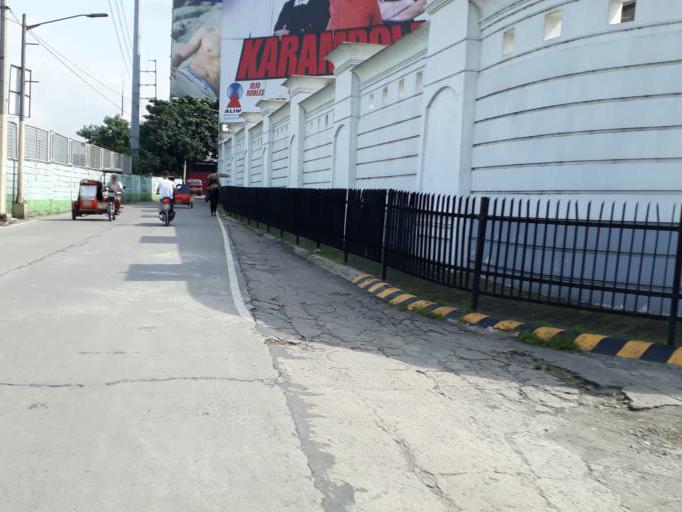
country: PH
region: Calabarzon
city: Bagong Pagasa
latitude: 14.6701
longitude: 121.0007
